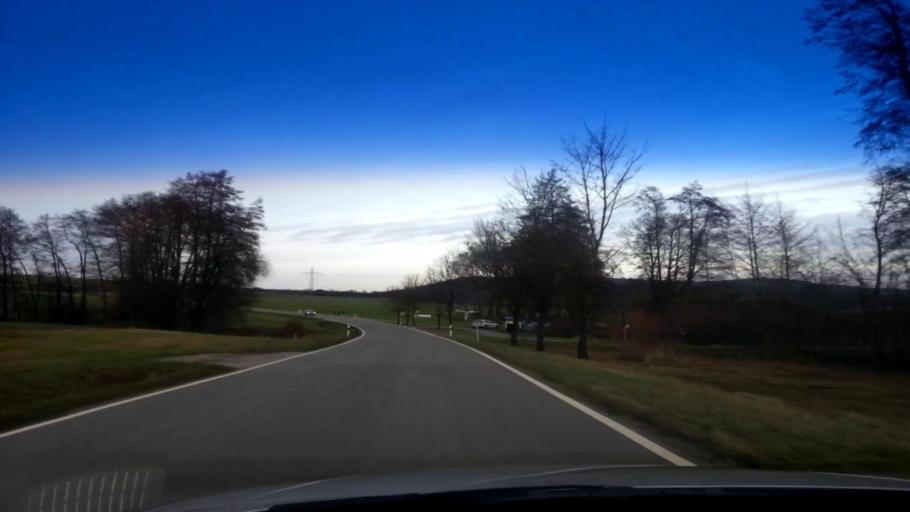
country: DE
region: Bavaria
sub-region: Upper Franconia
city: Strullendorf
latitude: 49.8690
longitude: 11.0022
